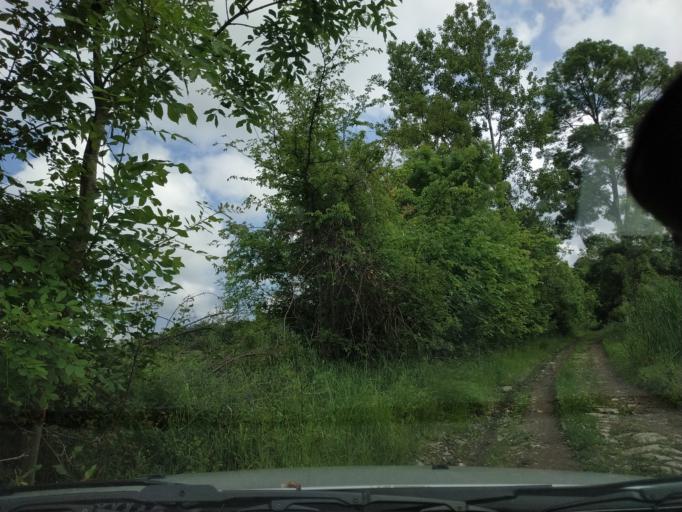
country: RS
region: Central Serbia
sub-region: Nisavski Okrug
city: Aleksinac
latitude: 43.4255
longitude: 21.5892
